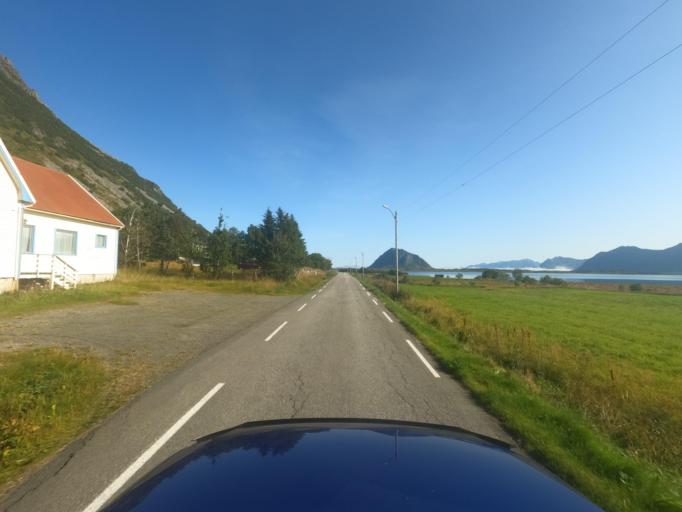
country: NO
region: Nordland
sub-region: Vestvagoy
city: Evjen
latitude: 68.3002
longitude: 14.0069
